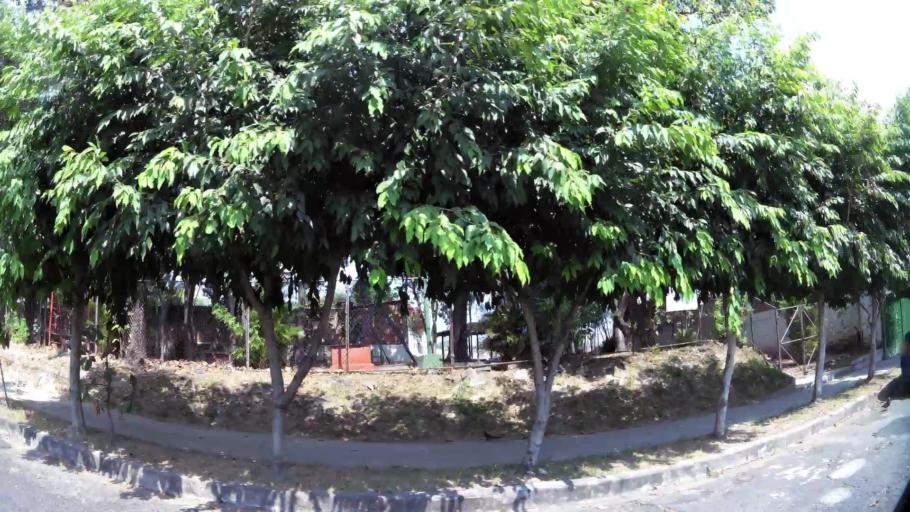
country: SV
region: San Salvador
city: Mejicanos
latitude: 13.7160
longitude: -89.2195
